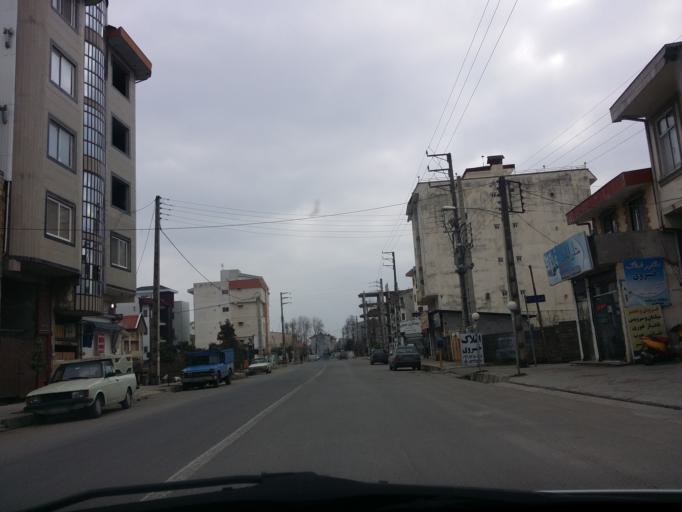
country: IR
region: Mazandaran
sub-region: Nowshahr
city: Nowshahr
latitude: 36.6422
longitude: 51.4879
